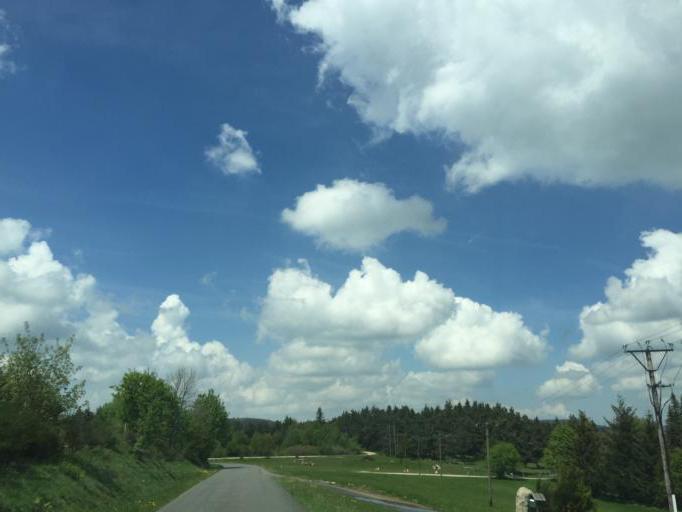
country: FR
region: Rhone-Alpes
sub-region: Departement de la Loire
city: Saint-Sauveur-en-Rue
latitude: 45.2923
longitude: 4.4821
